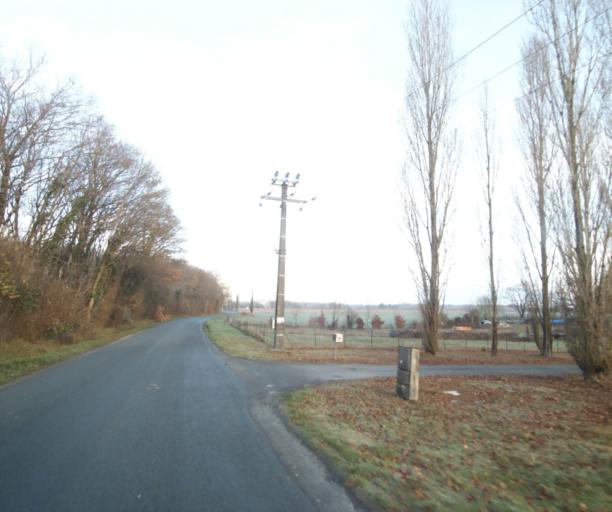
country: FR
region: Poitou-Charentes
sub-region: Departement de la Charente-Maritime
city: Saint-Hilaire-de-Villefranche
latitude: 45.8090
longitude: -0.5564
